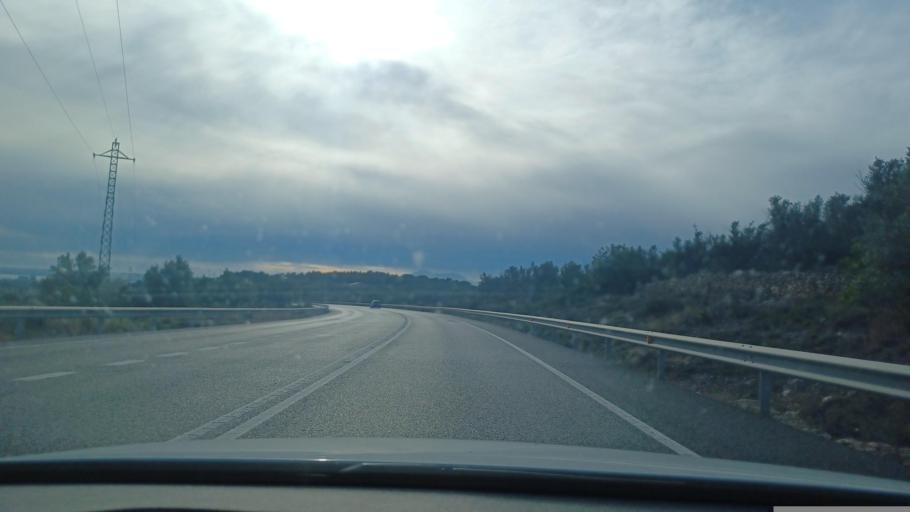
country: ES
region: Catalonia
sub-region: Provincia de Tarragona
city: El Perello
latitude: 40.8548
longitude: 0.7136
